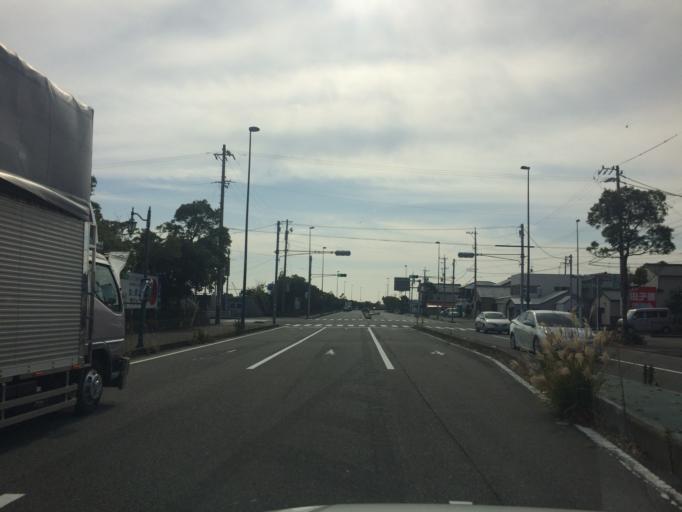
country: JP
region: Shizuoka
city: Yaizu
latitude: 34.8584
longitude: 138.3245
